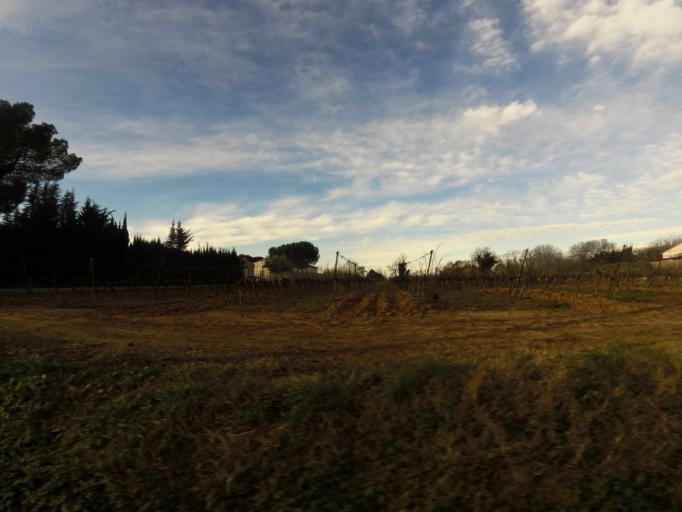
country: FR
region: Languedoc-Roussillon
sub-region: Departement du Gard
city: Mus
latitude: 43.7189
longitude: 4.1970
